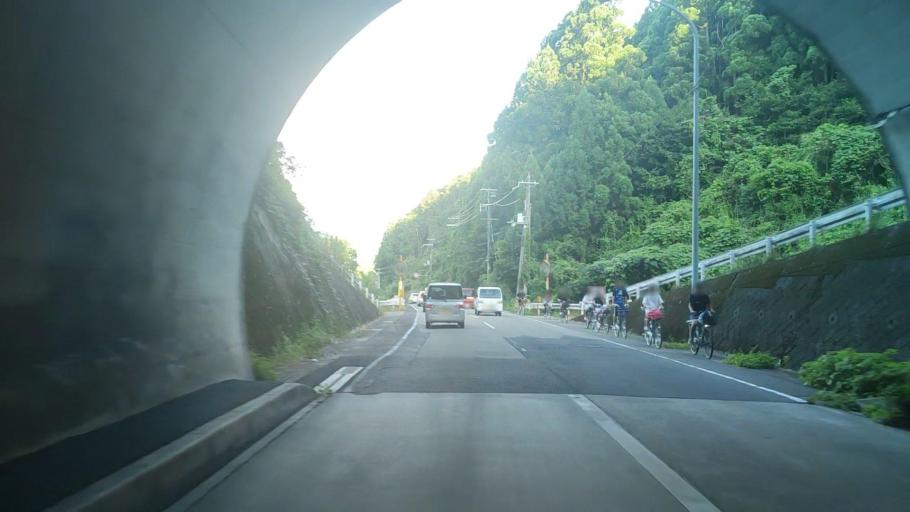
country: JP
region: Wakayama
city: Tanabe
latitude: 33.7282
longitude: 135.4367
